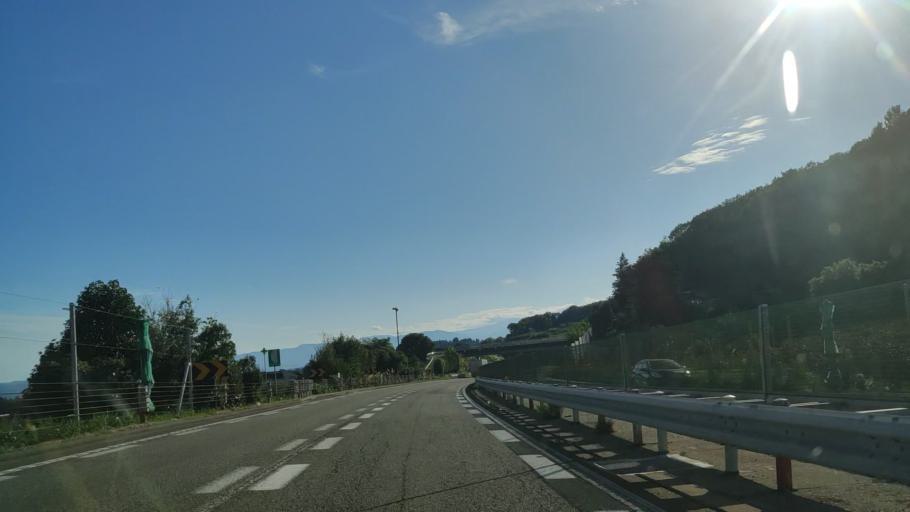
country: JP
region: Nagano
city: Iida
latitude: 35.5706
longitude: 137.8737
